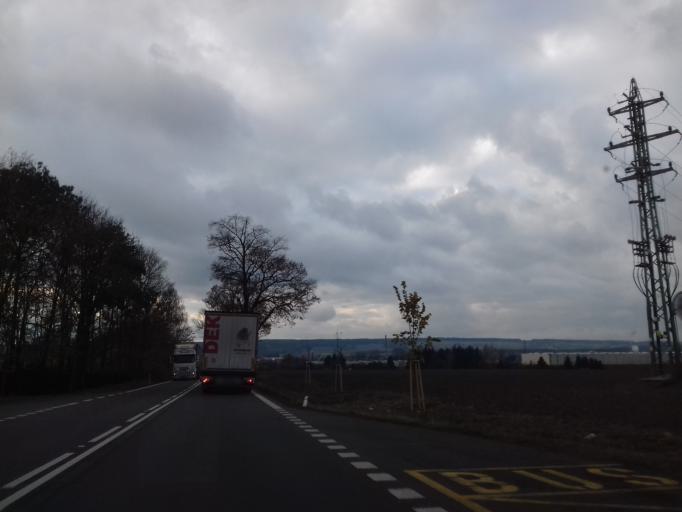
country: CZ
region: Pardubicky
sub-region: Okres Svitavy
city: Svitavy
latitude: 49.7598
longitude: 16.4953
